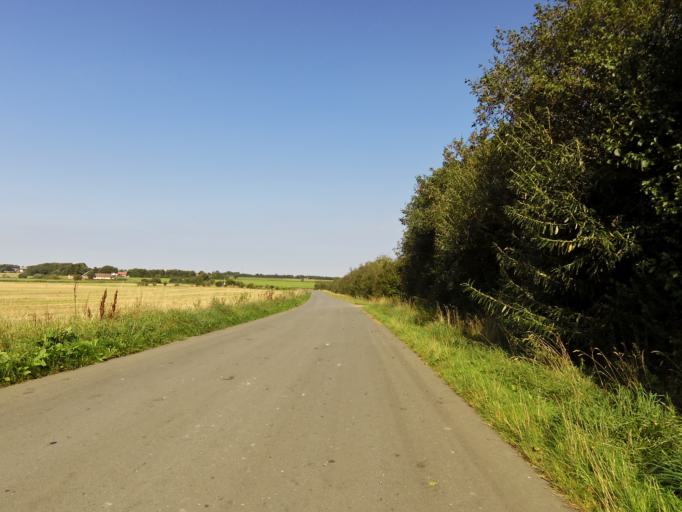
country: DK
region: South Denmark
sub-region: Vejen Kommune
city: Rodding
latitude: 55.3339
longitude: 9.1350
